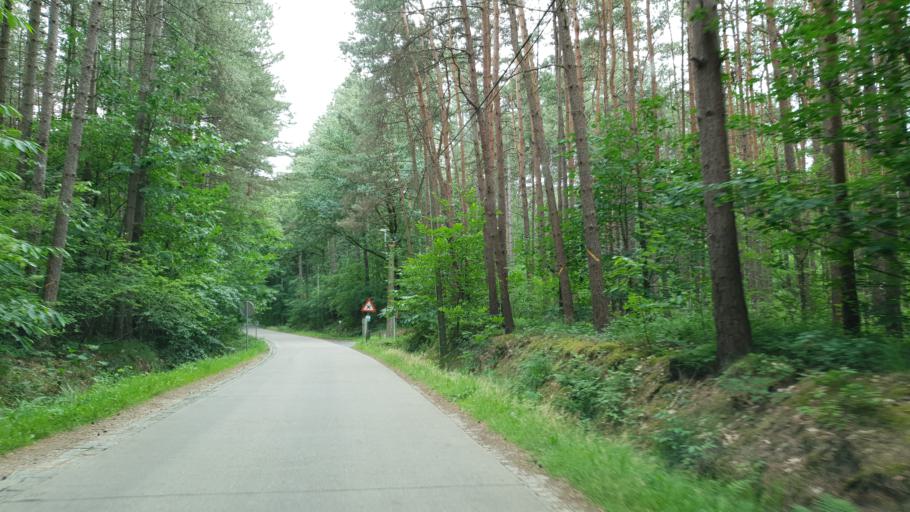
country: BE
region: Flanders
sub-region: Provincie Antwerpen
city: Herselt
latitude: 51.0578
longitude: 4.9017
